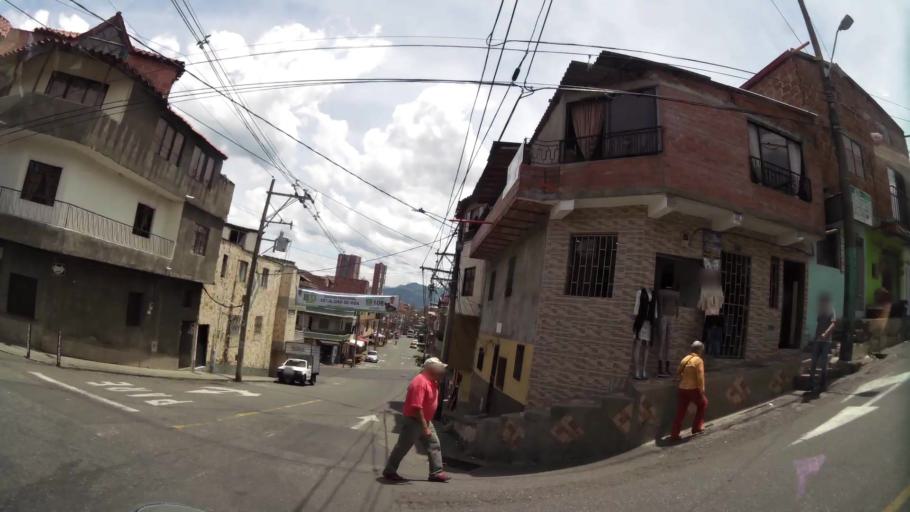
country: CO
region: Antioquia
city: Bello
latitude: 6.3404
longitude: -75.5591
